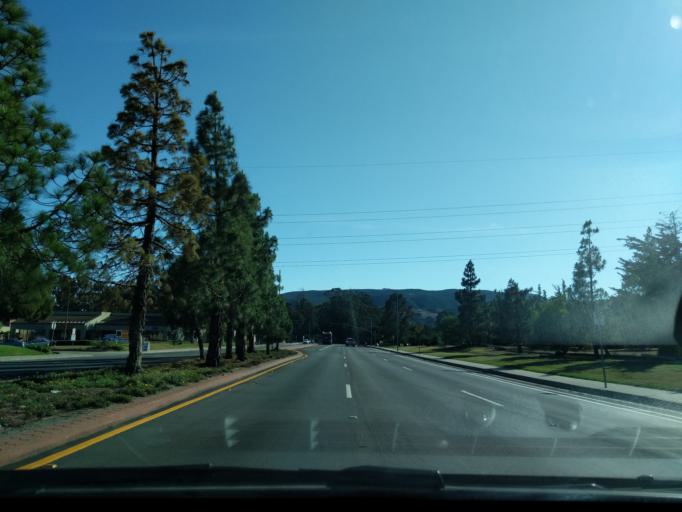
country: US
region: California
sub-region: San Luis Obispo County
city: San Luis Obispo
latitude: 35.2625
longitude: -120.6785
